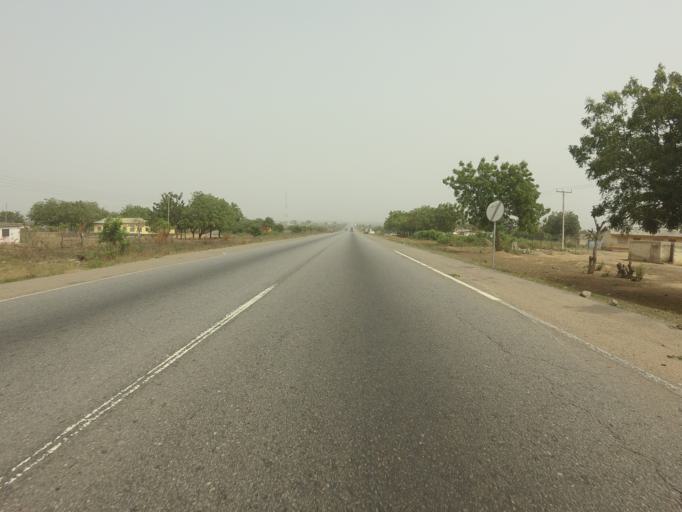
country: GH
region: Greater Accra
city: Tema
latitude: 5.8663
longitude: 0.2926
